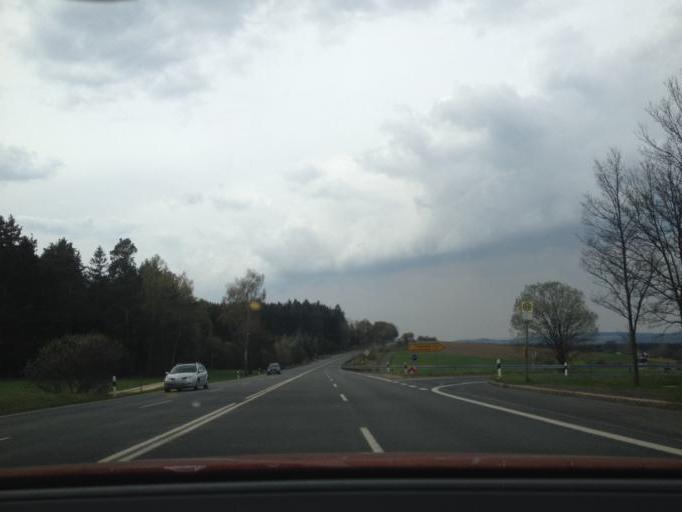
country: DE
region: Bavaria
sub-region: Upper Palatinate
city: Waldershof
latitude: 50.0128
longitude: 12.0520
